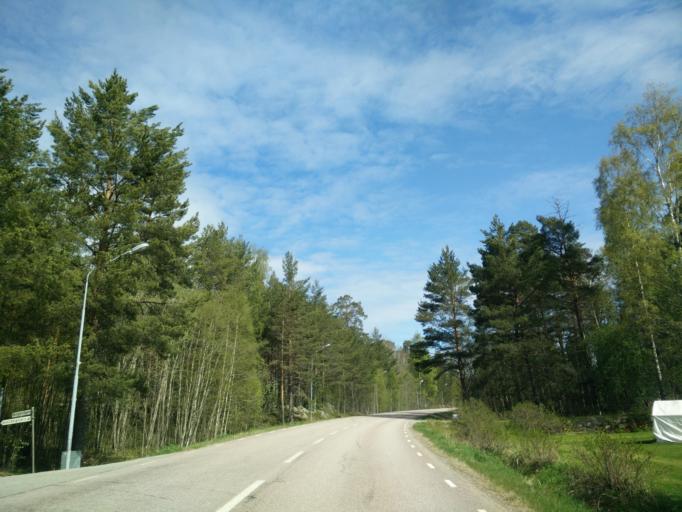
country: SE
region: Gaevleborg
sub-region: Hudiksvalls Kommun
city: Hudiksvall
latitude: 61.8664
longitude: 17.3126
